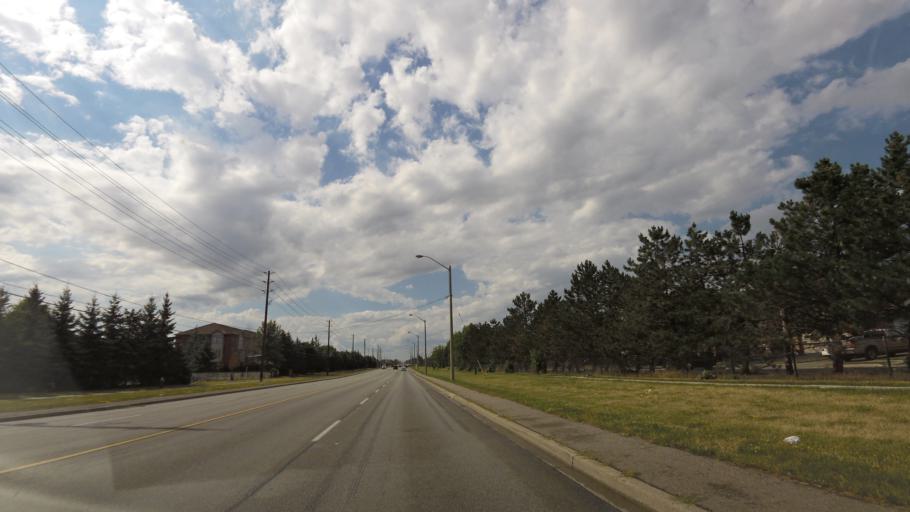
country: CA
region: Ontario
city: Brampton
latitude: 43.6930
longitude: -79.7934
